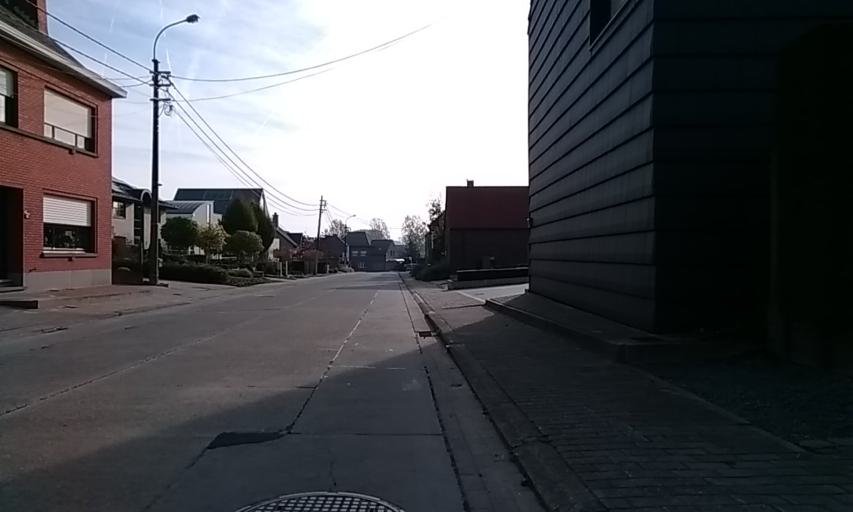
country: BE
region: Flanders
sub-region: Provincie Oost-Vlaanderen
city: Sint-Lievens-Houtem
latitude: 50.9223
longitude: 3.8429
